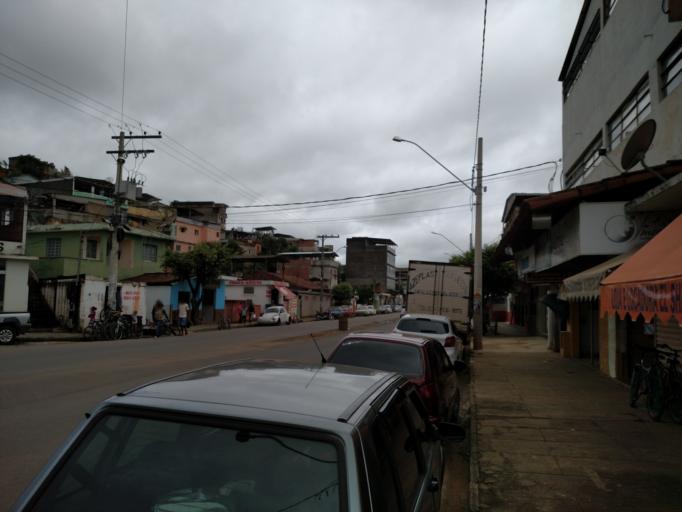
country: BR
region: Minas Gerais
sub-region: Leopoldina
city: Leopoldina
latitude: -21.5216
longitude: -42.6348
